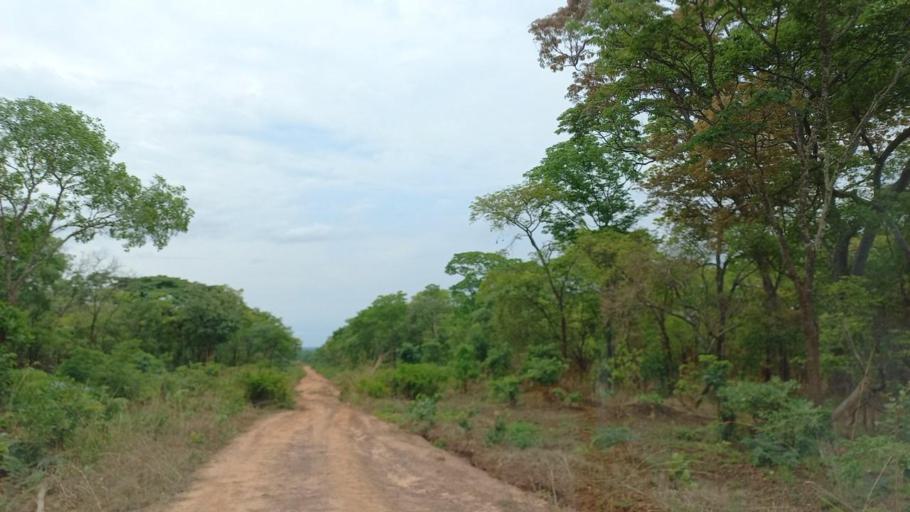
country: ZM
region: North-Western
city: Kalengwa
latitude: -13.6204
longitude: 24.9766
